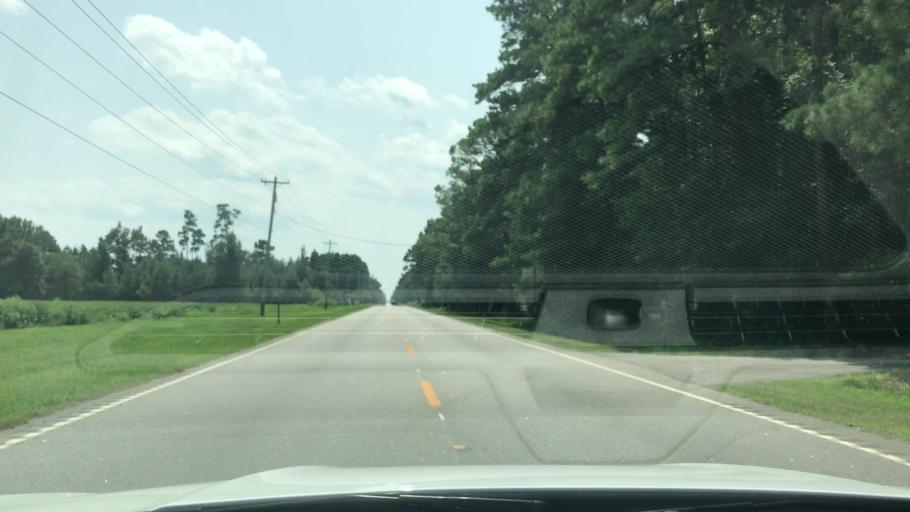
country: US
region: South Carolina
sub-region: Horry County
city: Conway
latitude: 33.7671
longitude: -79.0729
